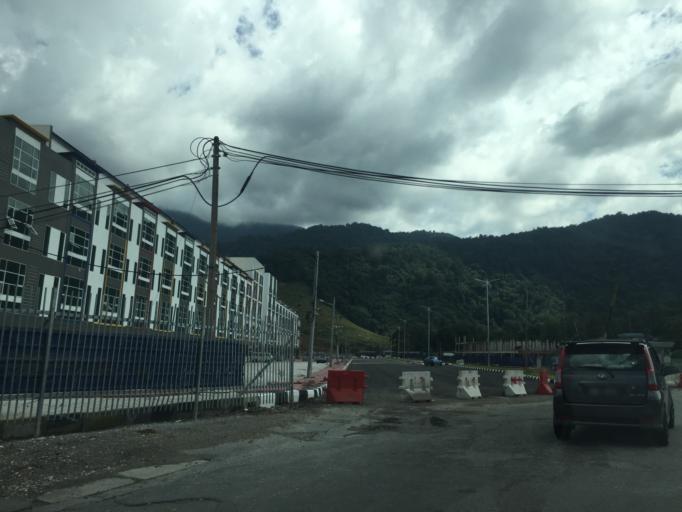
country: MY
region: Perak
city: Kampar
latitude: 4.3249
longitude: 101.1508
